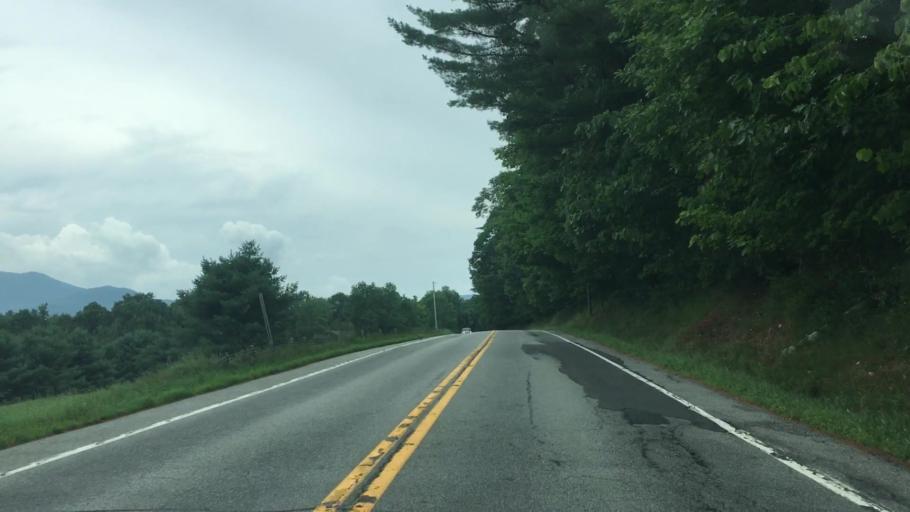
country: US
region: New York
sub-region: Essex County
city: Elizabethtown
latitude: 44.3995
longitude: -73.7075
